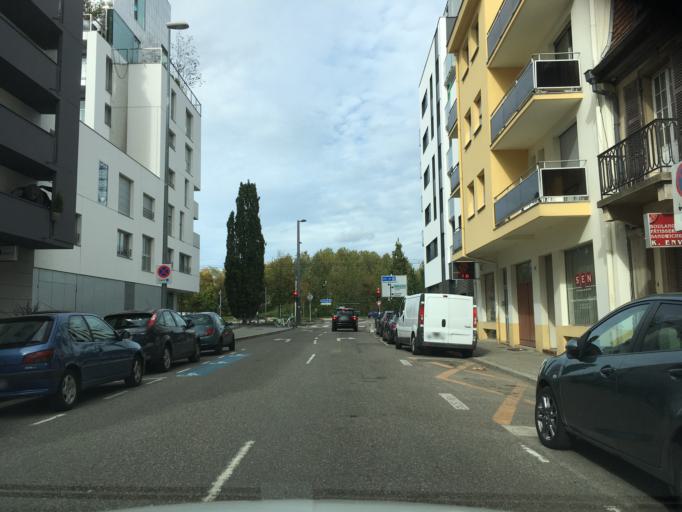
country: FR
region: Alsace
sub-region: Departement du Bas-Rhin
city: Strasbourg
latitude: 48.5710
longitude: 7.7548
